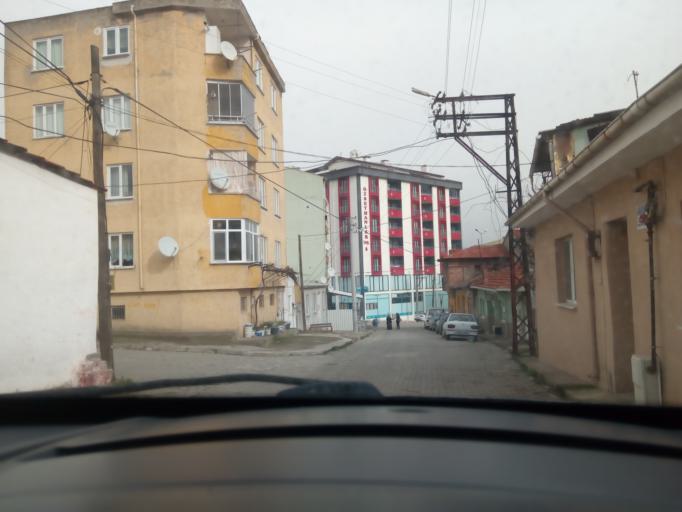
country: TR
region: Balikesir
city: Susurluk
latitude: 39.9098
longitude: 28.1580
